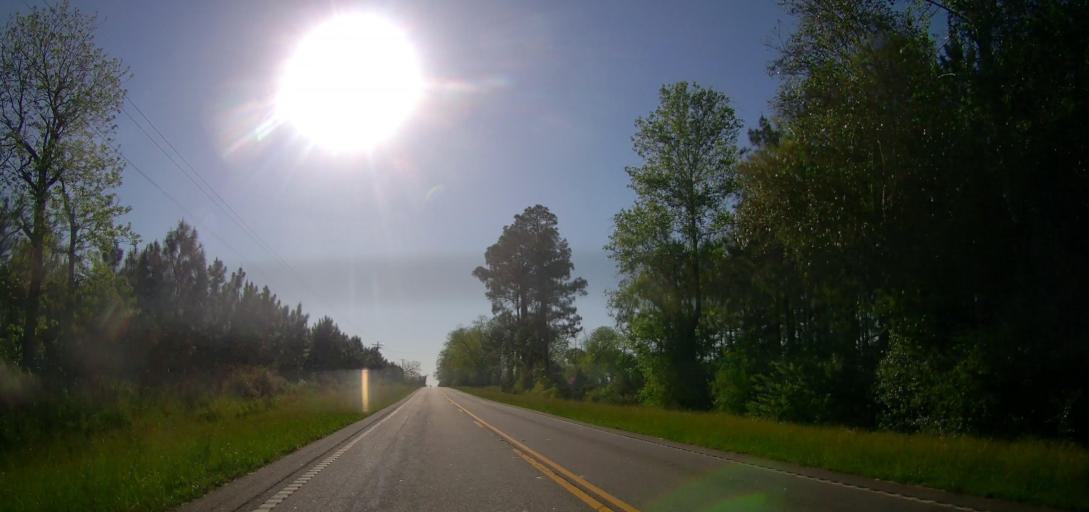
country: US
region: Georgia
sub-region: Ben Hill County
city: Fitzgerald
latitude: 31.7181
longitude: -83.3156
